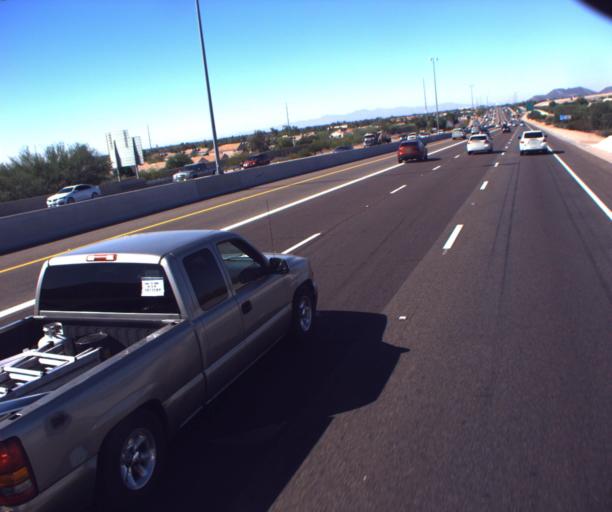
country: US
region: Arizona
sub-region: Maricopa County
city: Paradise Valley
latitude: 33.6692
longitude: -112.0517
